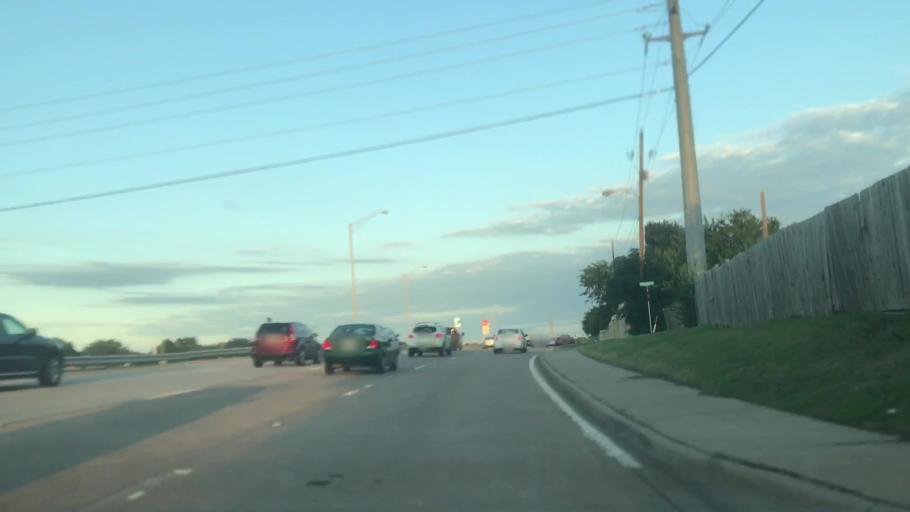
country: US
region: Texas
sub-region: Dallas County
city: Carrollton
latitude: 32.9851
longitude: -96.8888
